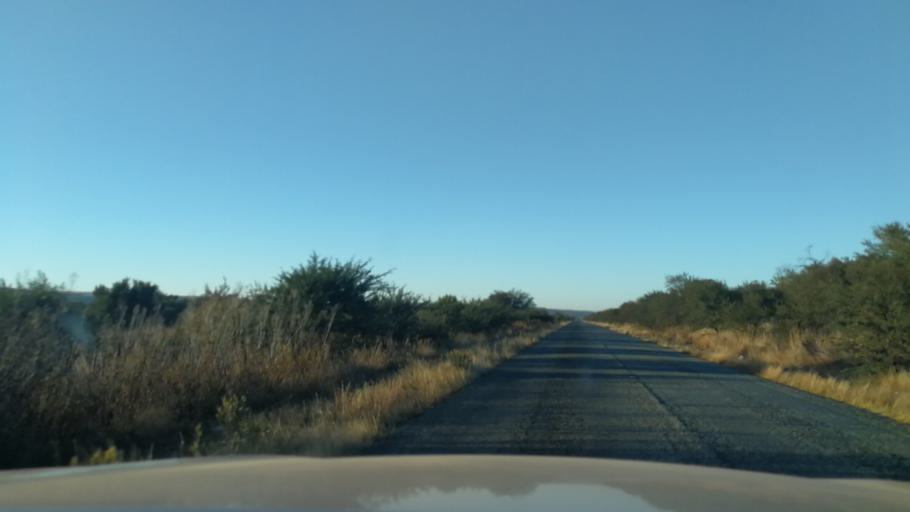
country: ZA
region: North-West
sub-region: Bojanala Platinum District Municipality
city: Koster
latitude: -25.6966
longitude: 26.7338
